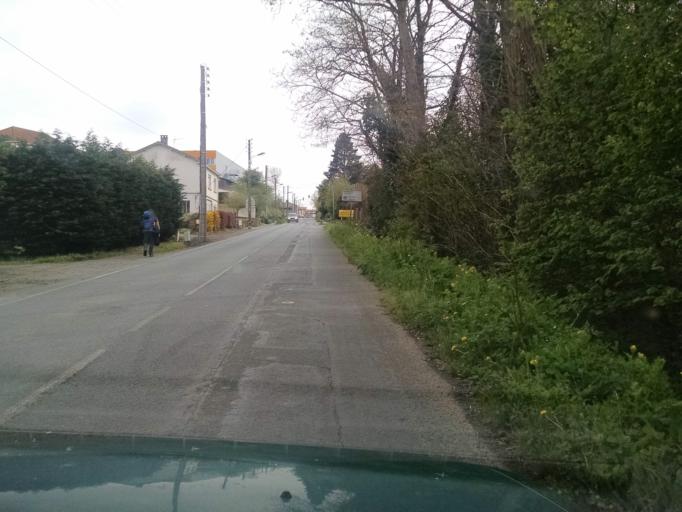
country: FR
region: Pays de la Loire
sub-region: Departement de la Loire-Atlantique
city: Gorges
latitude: 47.1052
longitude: -1.3048
